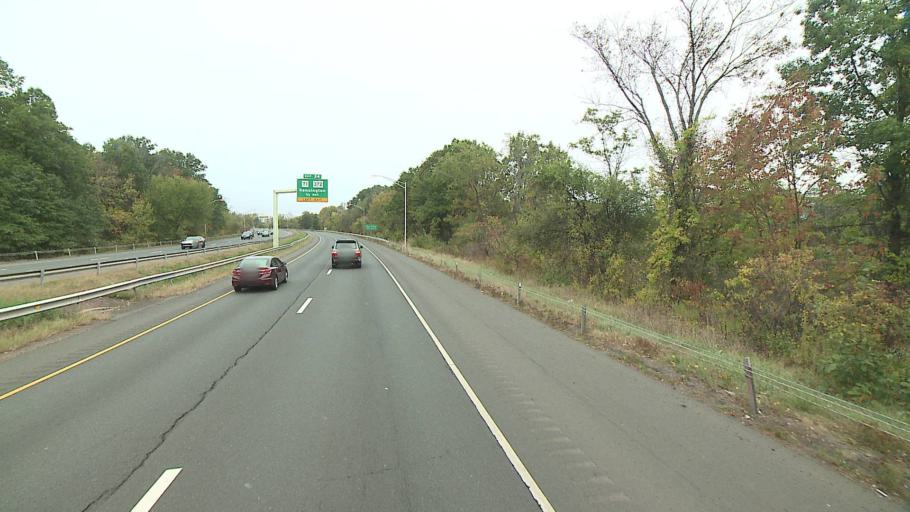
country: US
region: Connecticut
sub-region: Hartford County
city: Kensington
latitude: 41.6408
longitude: -72.7547
